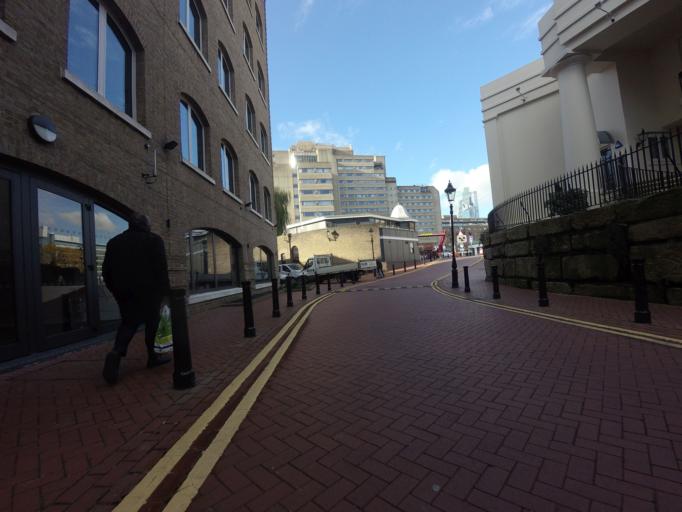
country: GB
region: England
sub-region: Greater London
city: City of London
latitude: 51.5062
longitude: -0.0714
